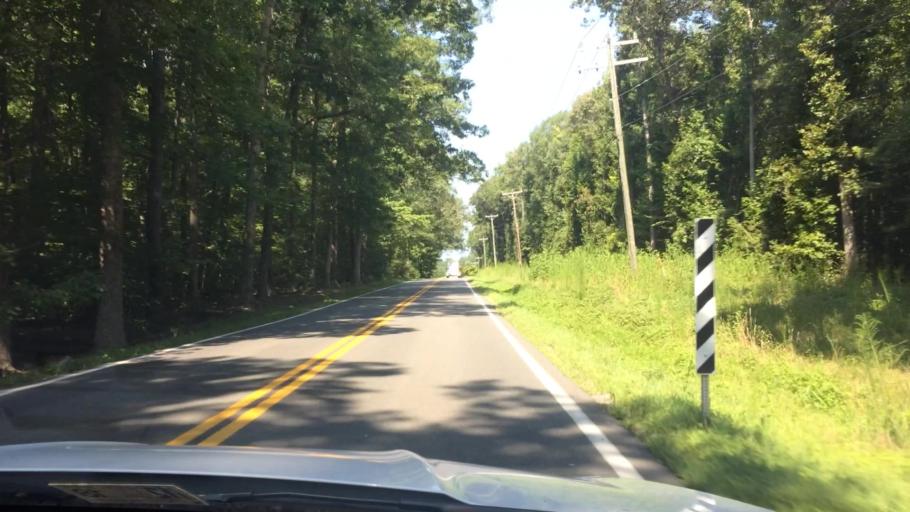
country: US
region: Virginia
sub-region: New Kent County
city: New Kent
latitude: 37.5210
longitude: -77.0023
